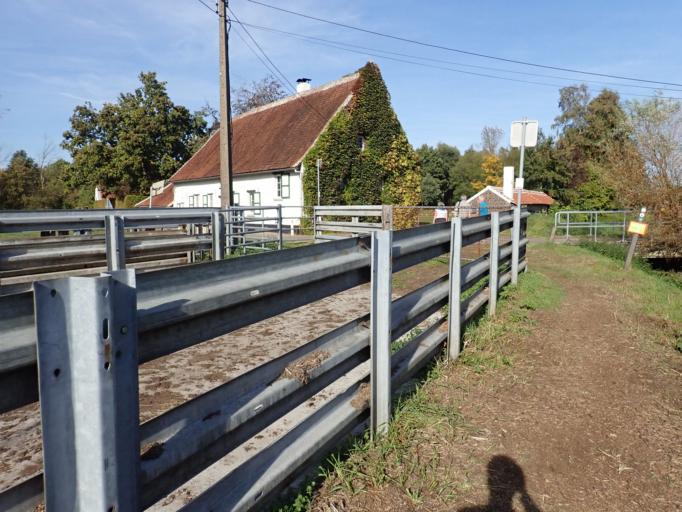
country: BE
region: Flanders
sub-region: Provincie Vlaams-Brabant
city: Holsbeek
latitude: 50.9341
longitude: 4.7645
